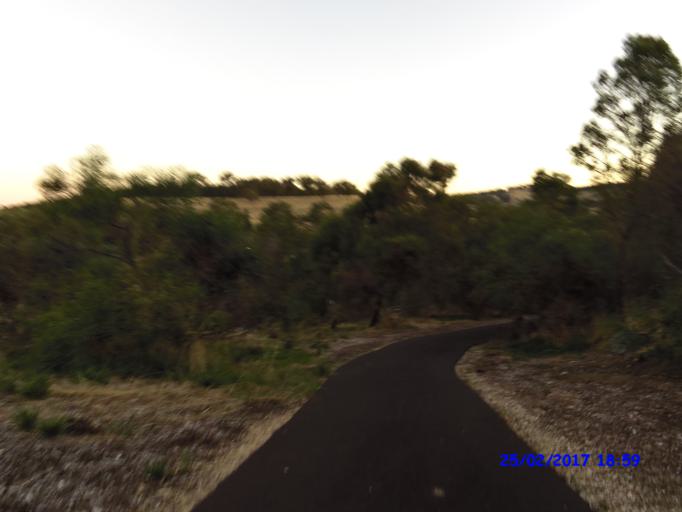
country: AU
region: Western Australia
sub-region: Harvey
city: Harvey
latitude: -33.0773
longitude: 115.9277
